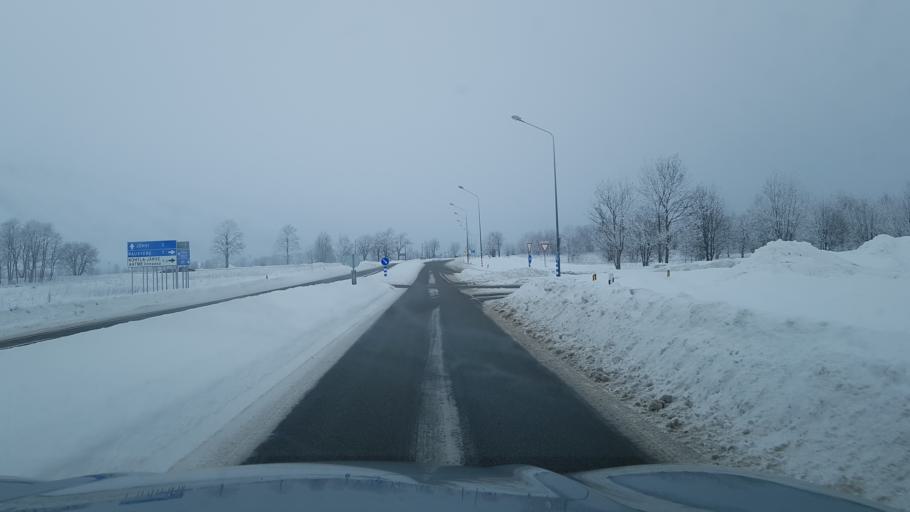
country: EE
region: Ida-Virumaa
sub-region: Johvi vald
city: Johvi
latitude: 59.3359
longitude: 27.4030
